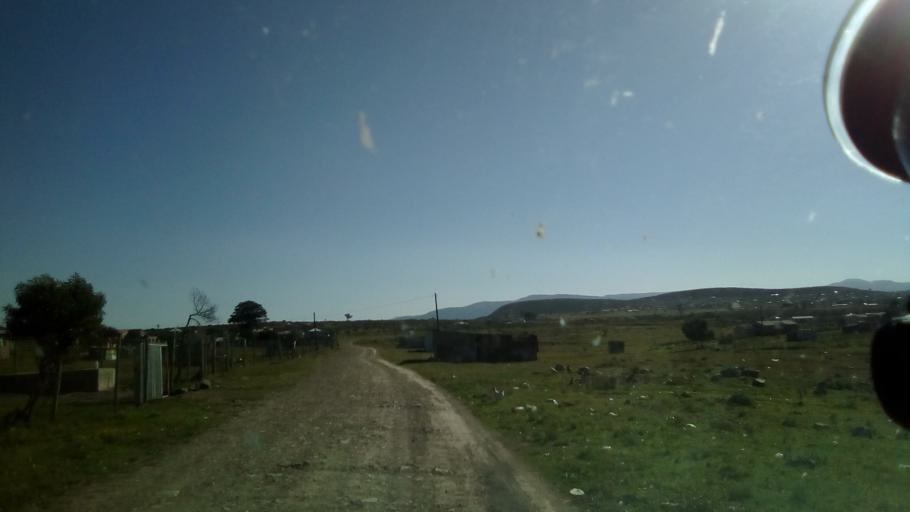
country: ZA
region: Eastern Cape
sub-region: Buffalo City Metropolitan Municipality
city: Bhisho
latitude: -32.8306
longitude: 27.3706
